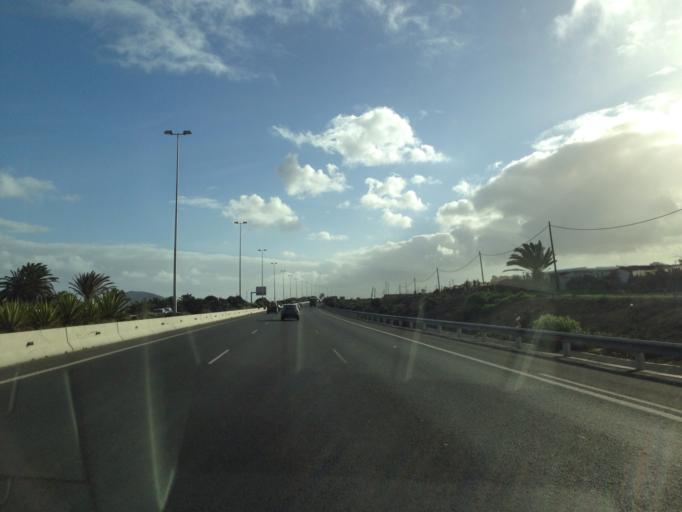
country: ES
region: Canary Islands
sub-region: Provincia de Las Palmas
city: Ingenio
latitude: 27.9150
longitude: -15.3986
